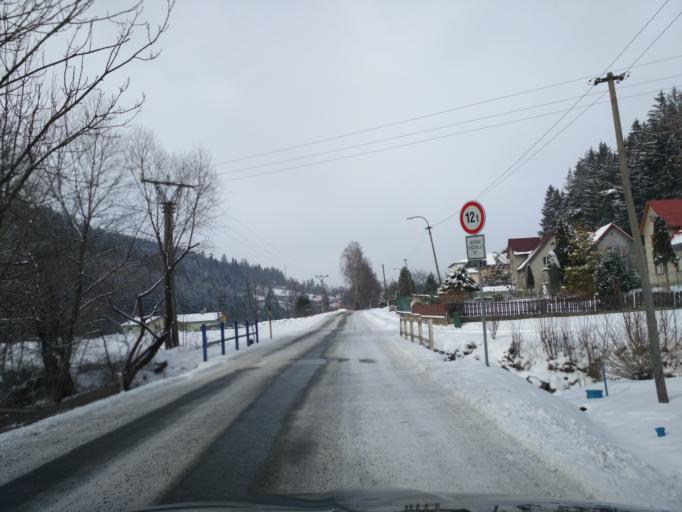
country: CZ
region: Zlin
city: Valasska Bystrice
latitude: 49.4095
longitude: 18.1174
